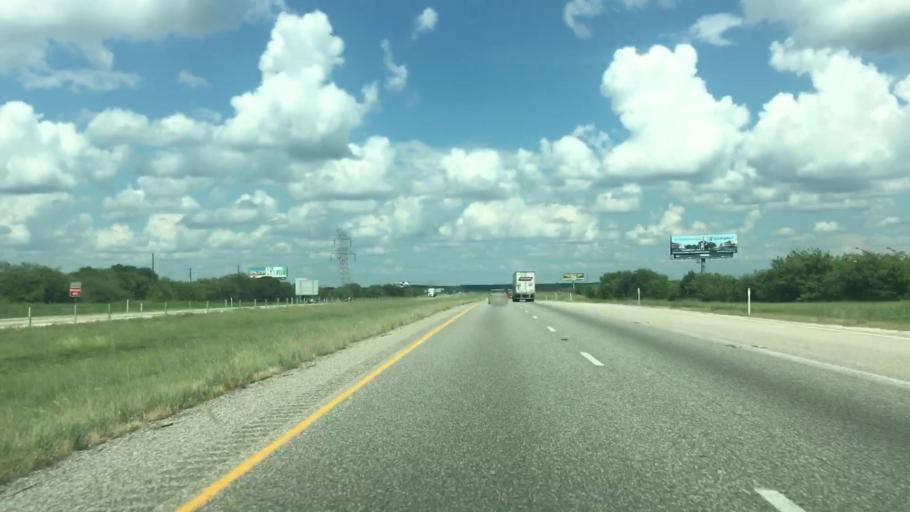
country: US
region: Texas
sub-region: Hill County
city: Hillsboro
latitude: 32.0794
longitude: -97.0510
